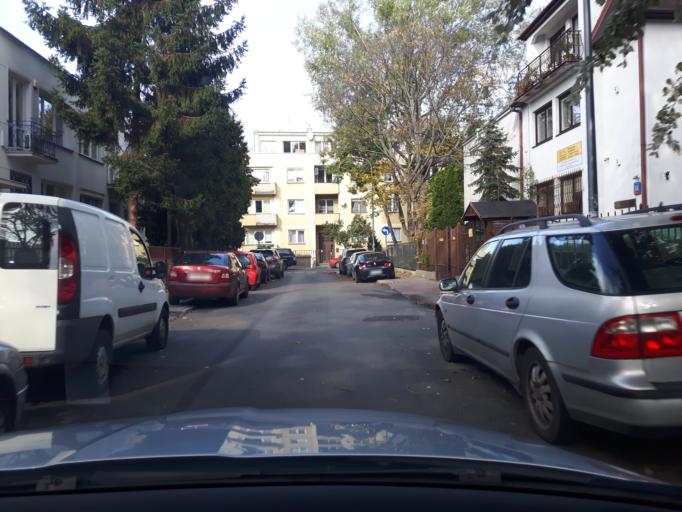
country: PL
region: Masovian Voivodeship
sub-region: Warszawa
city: Praga Poludnie
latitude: 52.2384
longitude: 21.0623
